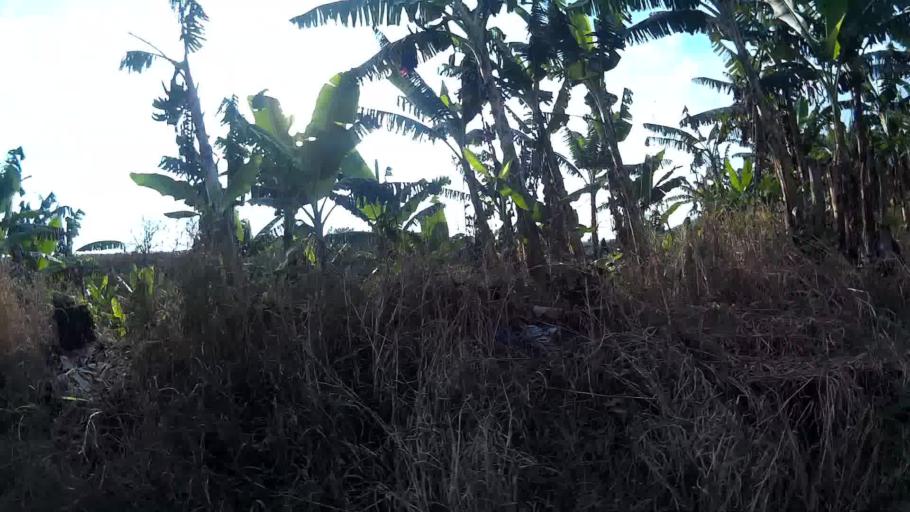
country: CO
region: Valle del Cauca
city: Ulloa
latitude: 4.7633
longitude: -75.7506
